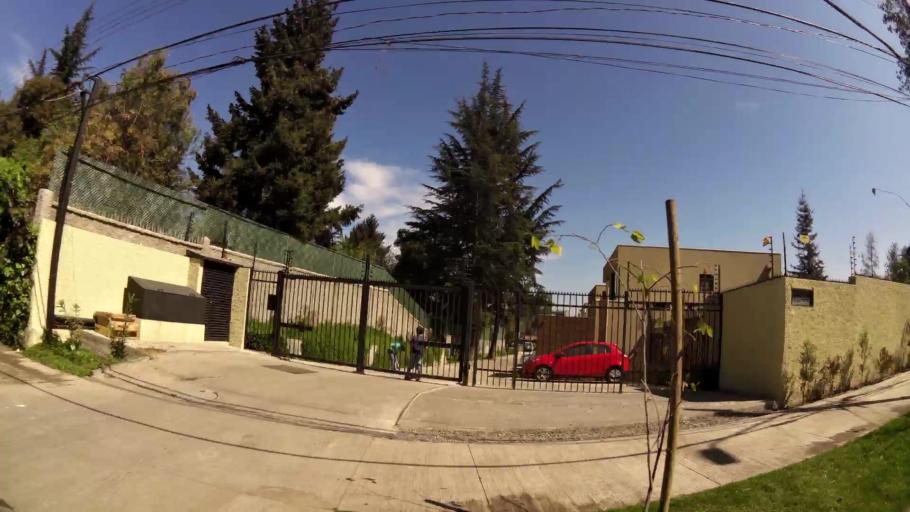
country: CL
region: Santiago Metropolitan
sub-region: Provincia de Santiago
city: Villa Presidente Frei, Nunoa, Santiago, Chile
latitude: -33.4416
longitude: -70.5246
